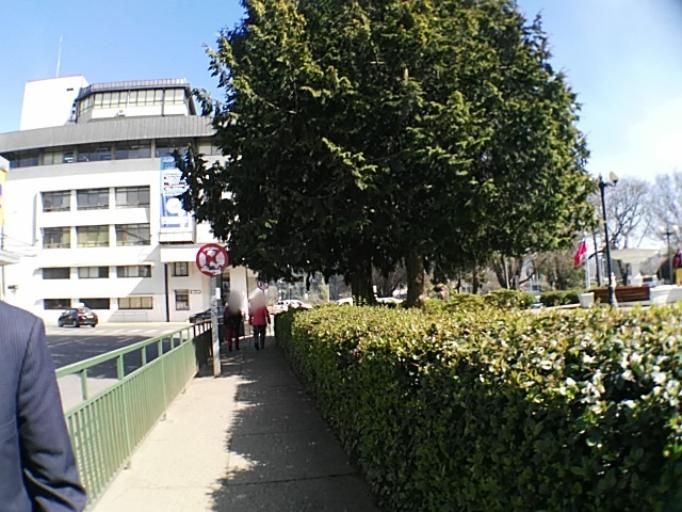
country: CL
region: Los Rios
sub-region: Provincia de Valdivia
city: Valdivia
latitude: -39.8128
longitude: -73.2461
